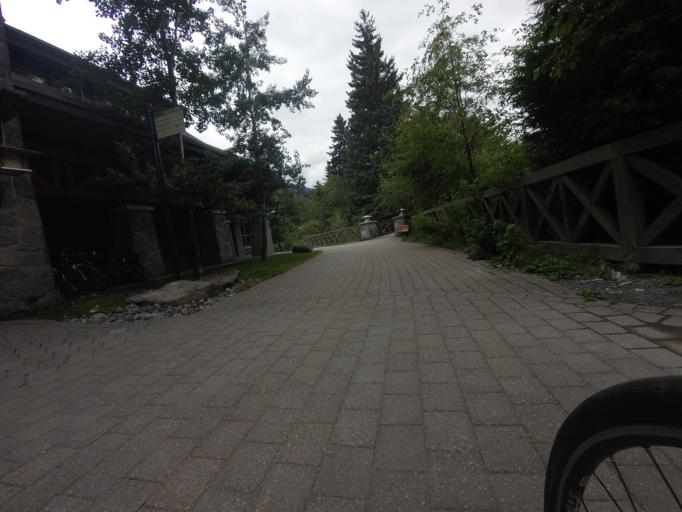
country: CA
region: British Columbia
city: Whistler
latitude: 50.0963
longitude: -122.9965
